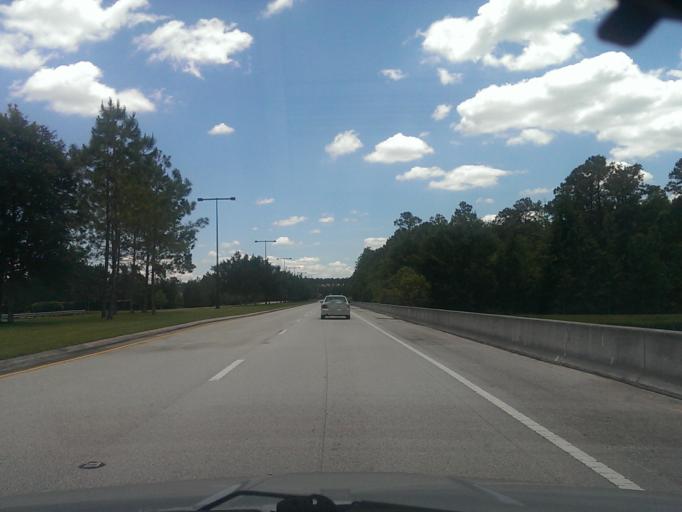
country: US
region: Florida
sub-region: Osceola County
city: Celebration
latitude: 28.3626
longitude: -81.5795
